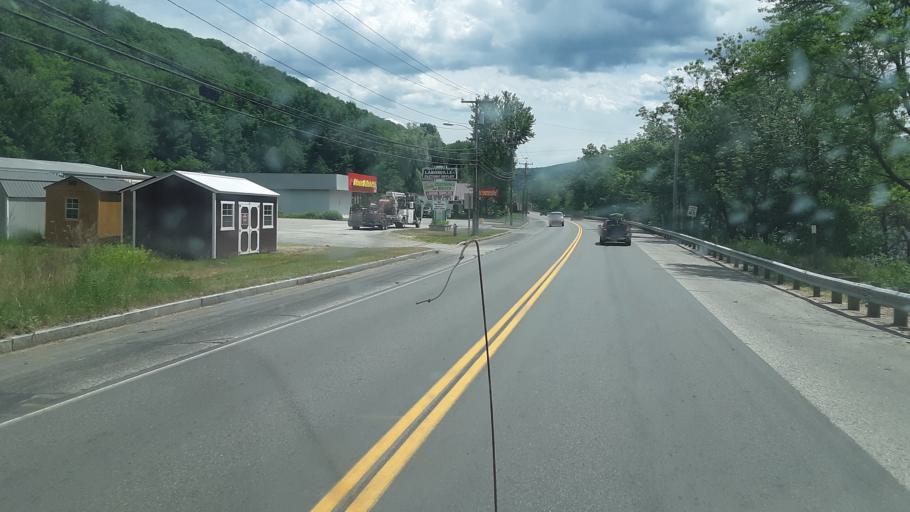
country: US
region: Maine
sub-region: Oxford County
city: Mexico
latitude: 44.5487
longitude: -70.5320
